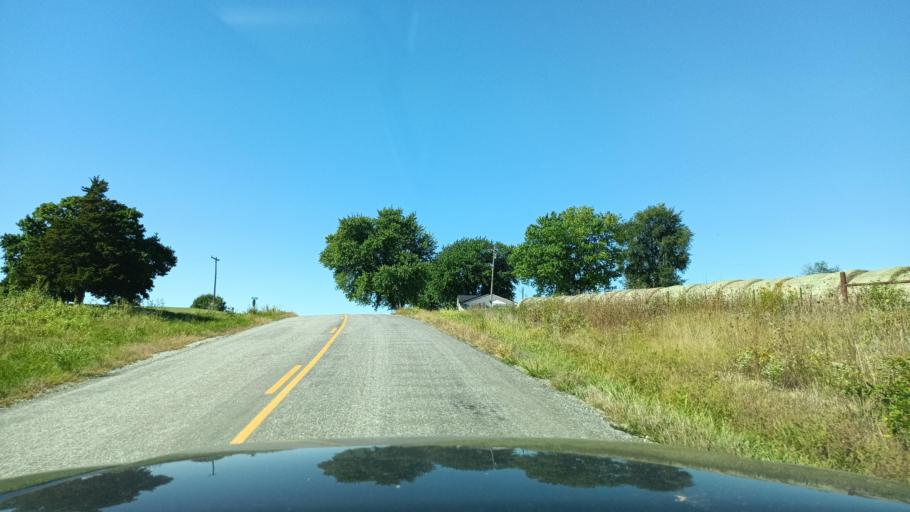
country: US
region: Missouri
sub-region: Adair County
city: Kirksville
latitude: 40.3307
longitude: -92.5146
